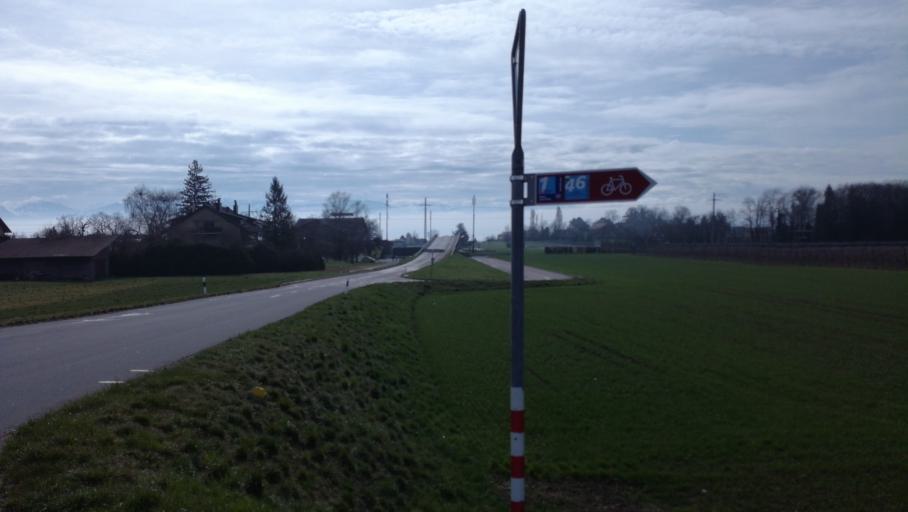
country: CH
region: Vaud
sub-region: Nyon District
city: Rolle
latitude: 46.4471
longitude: 6.3041
